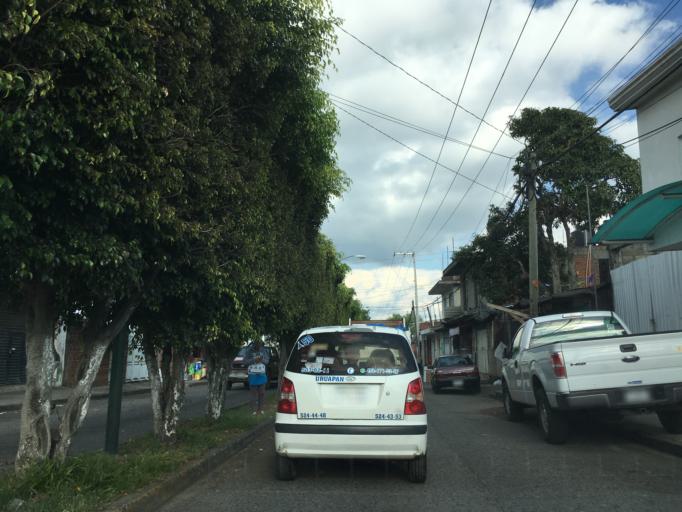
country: MX
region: Michoacan
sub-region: Uruapan
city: Uruapan
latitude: 19.4304
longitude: -102.0786
